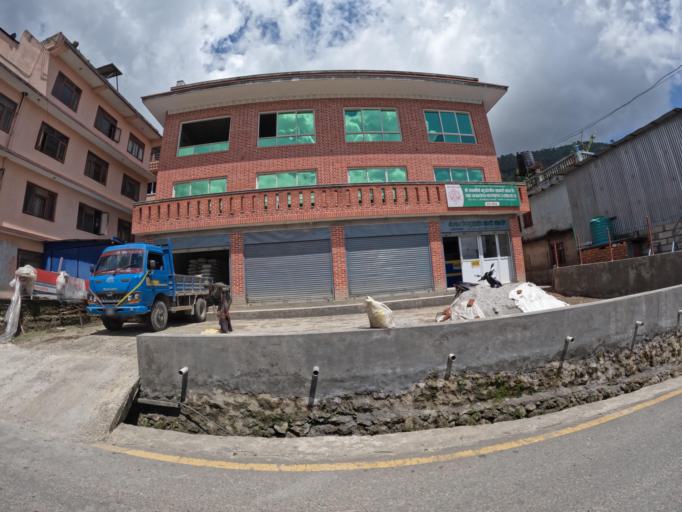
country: NP
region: Central Region
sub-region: Bagmati Zone
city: Kathmandu
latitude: 27.7920
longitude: 85.3302
